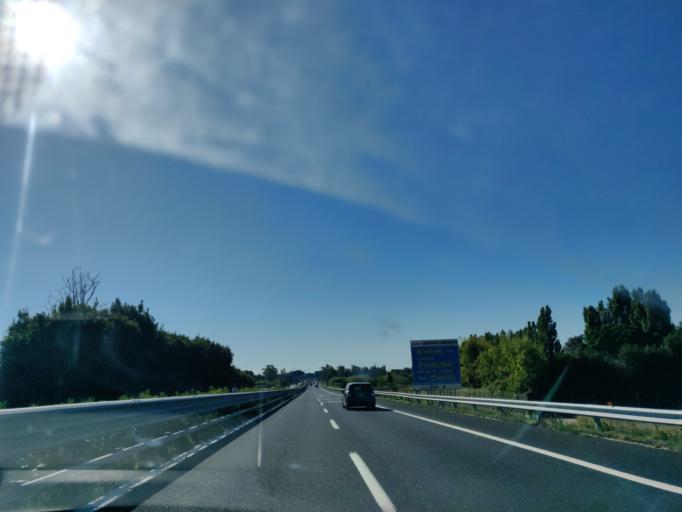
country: IT
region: Latium
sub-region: Citta metropolitana di Roma Capitale
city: Cerveteri
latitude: 41.9841
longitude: 12.0744
